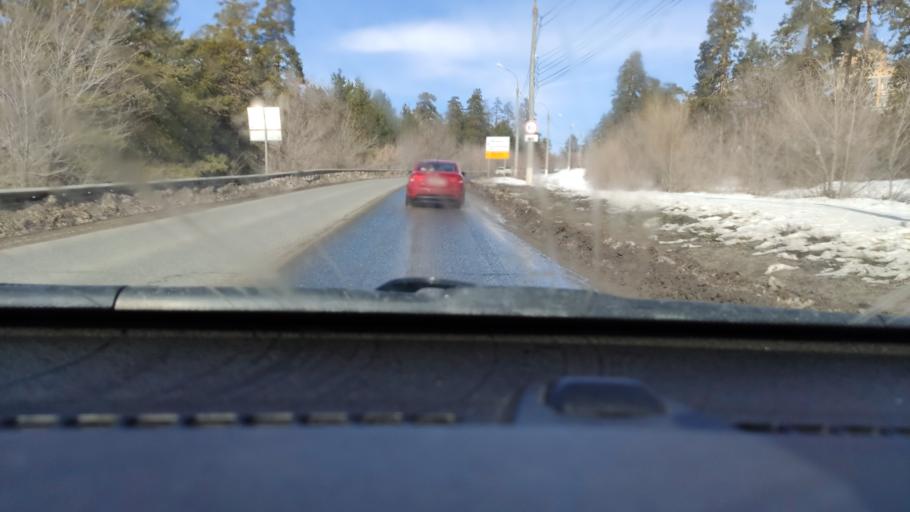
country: RU
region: Samara
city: Tol'yatti
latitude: 53.4784
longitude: 49.3261
